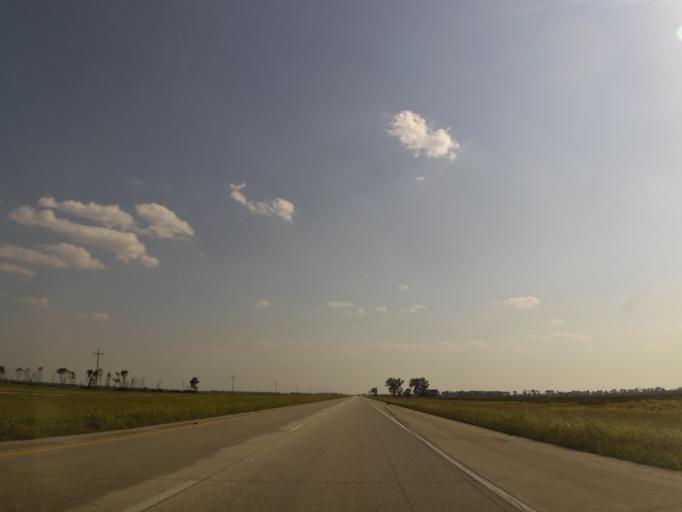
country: US
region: North Dakota
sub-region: Grand Forks County
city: Grand Forks
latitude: 48.1716
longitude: -97.1901
